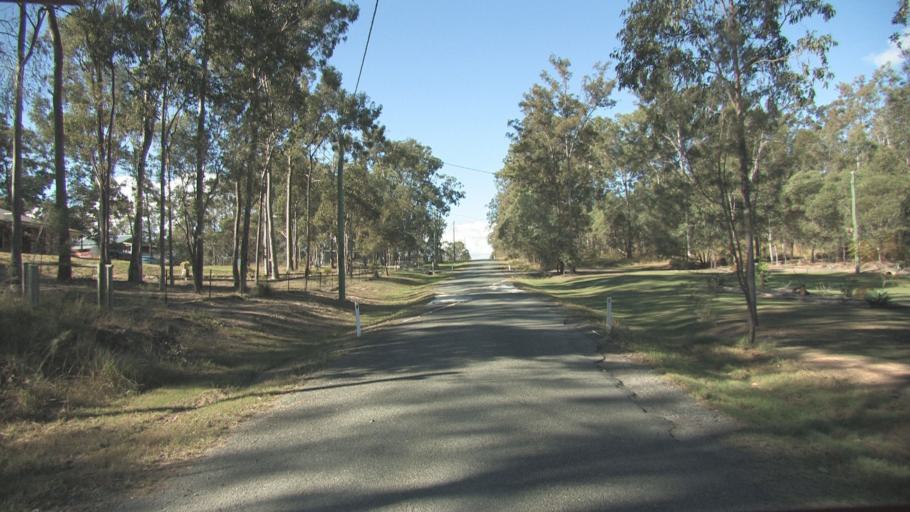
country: AU
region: Queensland
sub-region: Logan
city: Chambers Flat
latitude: -27.7977
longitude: 153.0783
